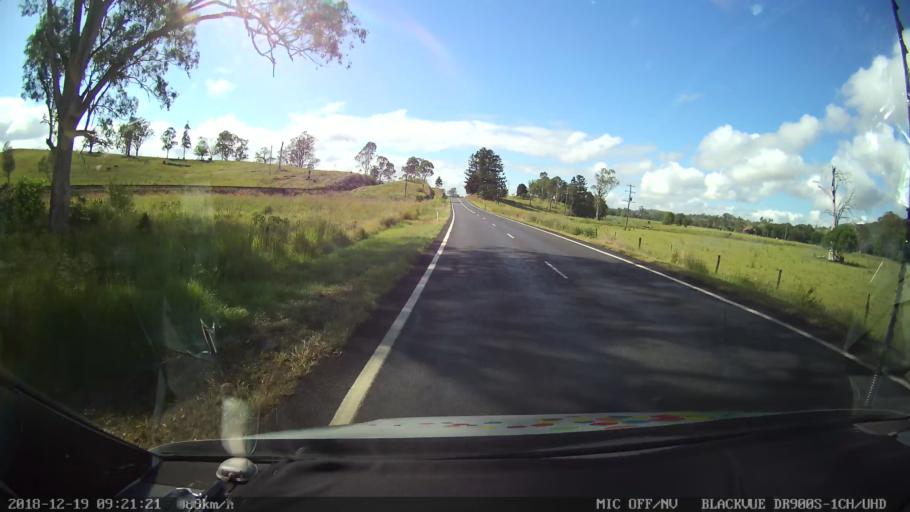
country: AU
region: New South Wales
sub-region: Kyogle
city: Kyogle
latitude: -28.5828
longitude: 152.9821
